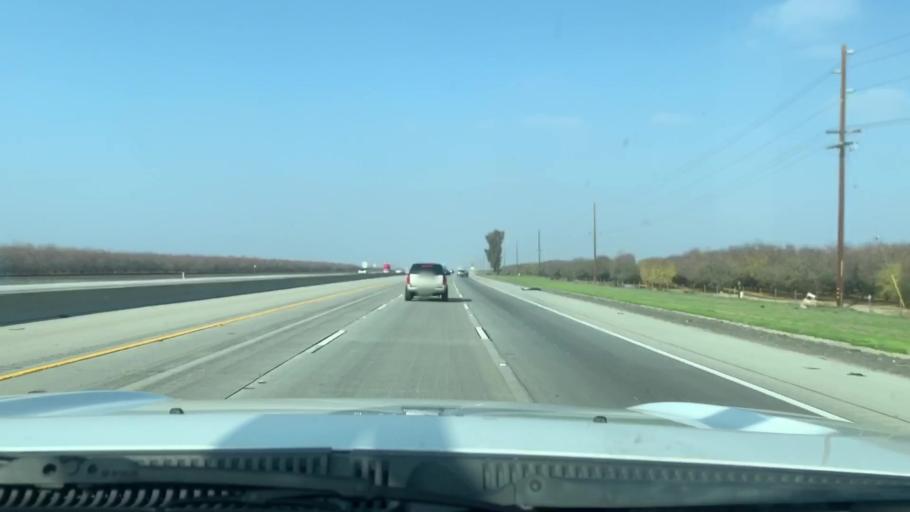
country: US
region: California
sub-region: Kern County
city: Shafter
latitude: 35.5382
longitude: -119.1932
